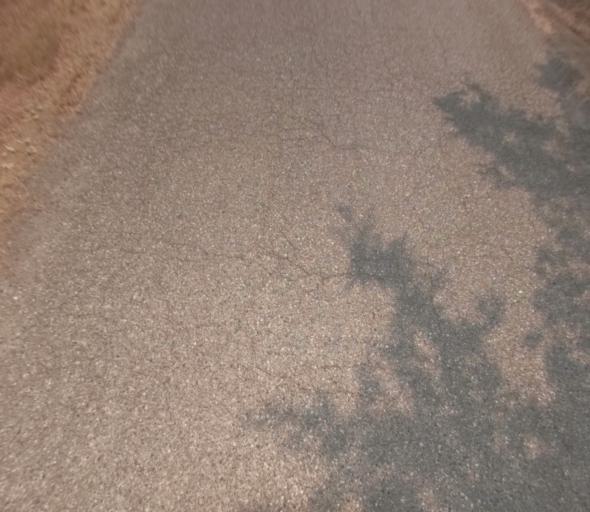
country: US
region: California
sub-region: Madera County
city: Coarsegold
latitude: 37.2124
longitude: -119.6843
